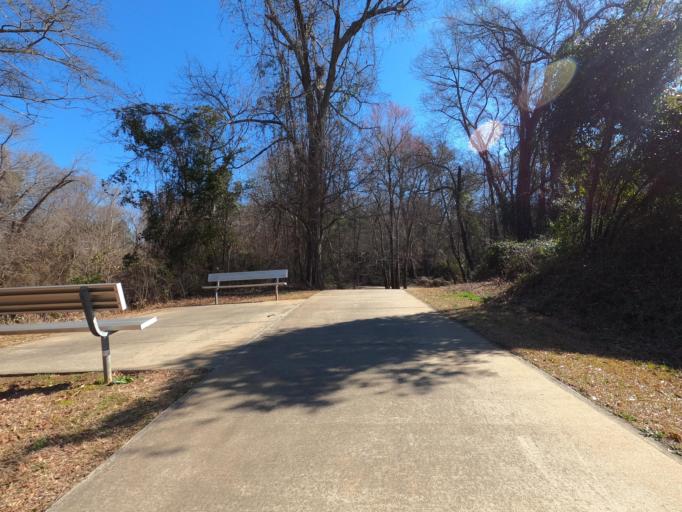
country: US
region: Georgia
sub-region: Clarke County
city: Athens
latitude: 33.9750
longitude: -83.3811
